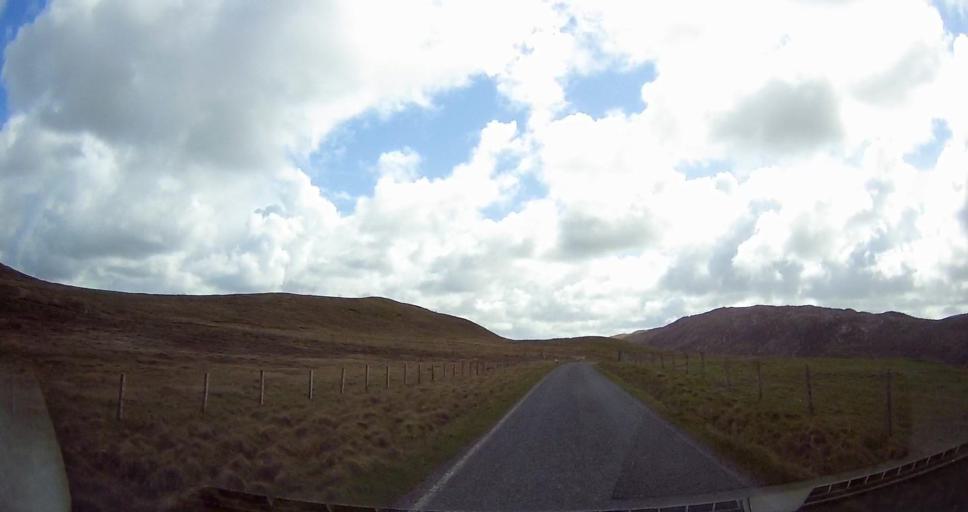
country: GB
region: Scotland
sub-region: Shetland Islands
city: Lerwick
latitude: 60.5597
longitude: -1.3351
